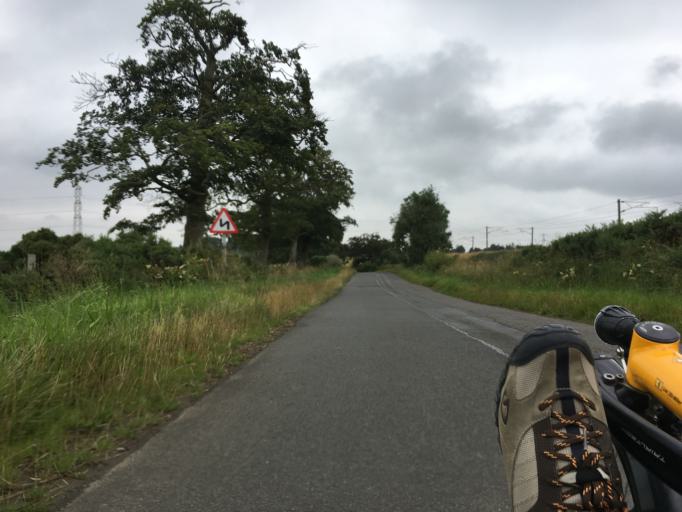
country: GB
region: Scotland
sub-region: West Lothian
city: Mid Calder
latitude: 55.8484
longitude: -3.5129
